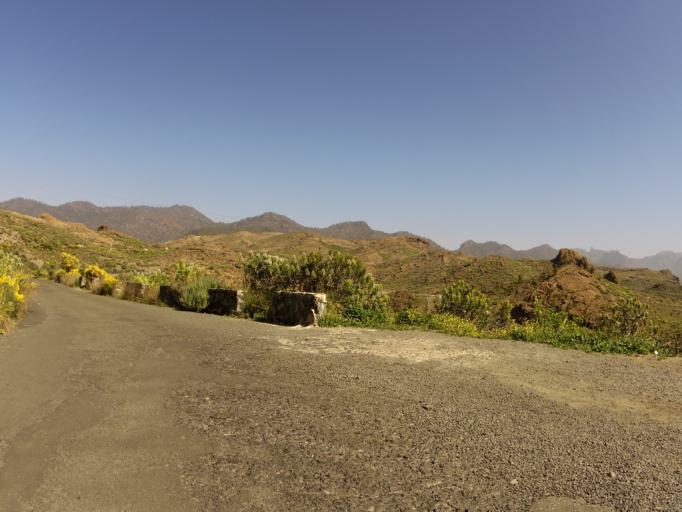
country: ES
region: Canary Islands
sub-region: Provincia de Las Palmas
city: Mogan
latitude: 27.9016
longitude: -15.6857
